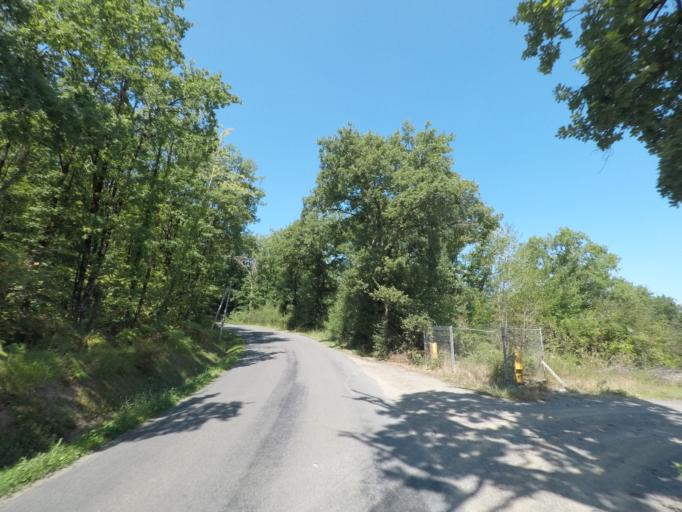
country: FR
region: Midi-Pyrenees
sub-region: Departement de l'Aveyron
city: Livinhac-le-Haut
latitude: 44.6082
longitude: 2.2284
